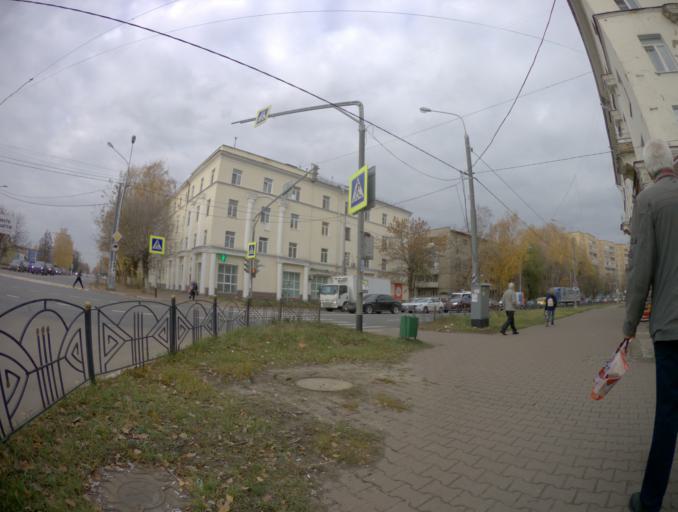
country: RU
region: Moskovskaya
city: Orekhovo-Zuyevo
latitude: 55.8058
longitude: 38.9692
